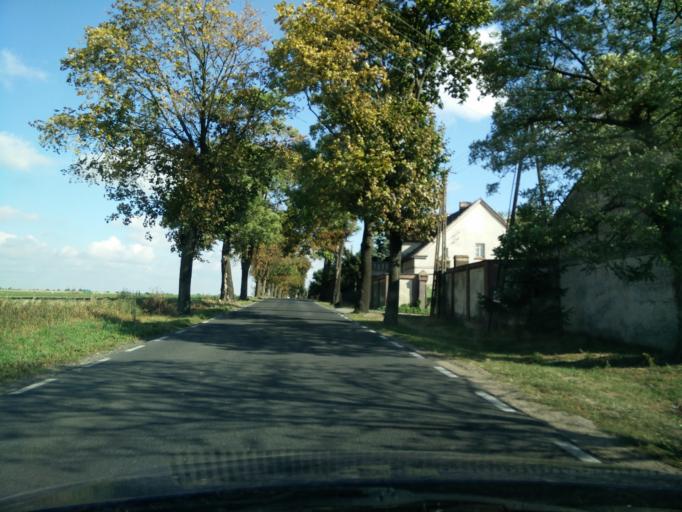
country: PL
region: Greater Poland Voivodeship
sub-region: Powiat sredzki
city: Sroda Wielkopolska
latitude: 52.2448
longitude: 17.2922
